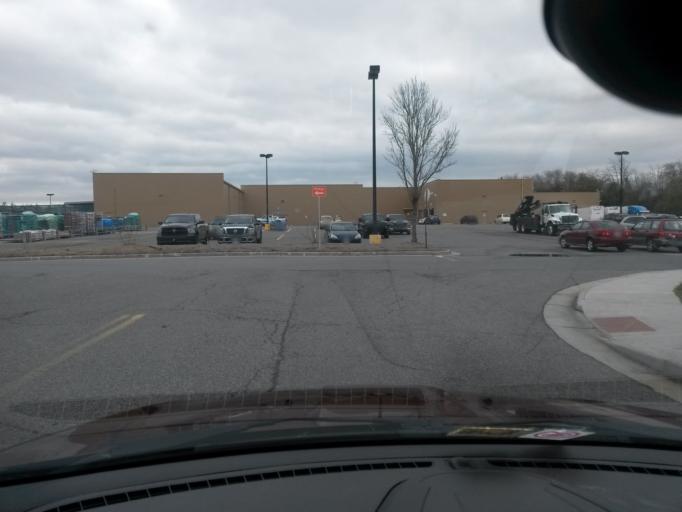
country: US
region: Virginia
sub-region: Montgomery County
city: Merrimac
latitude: 37.1621
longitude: -80.4268
